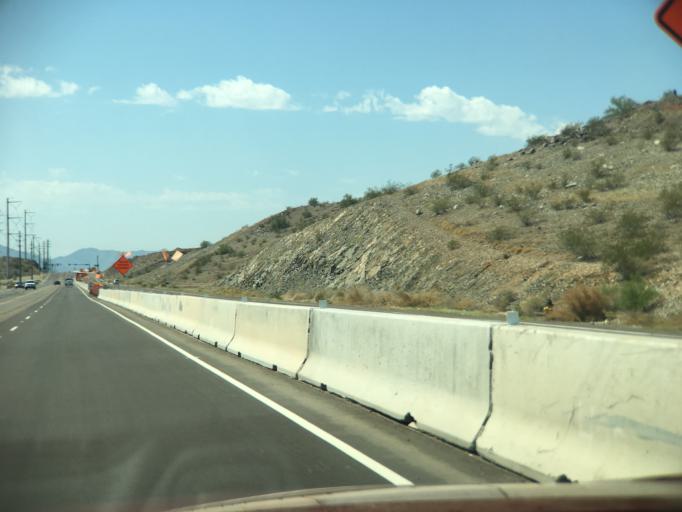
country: US
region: Arizona
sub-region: Maricopa County
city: Guadalupe
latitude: 33.2912
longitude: -112.0550
